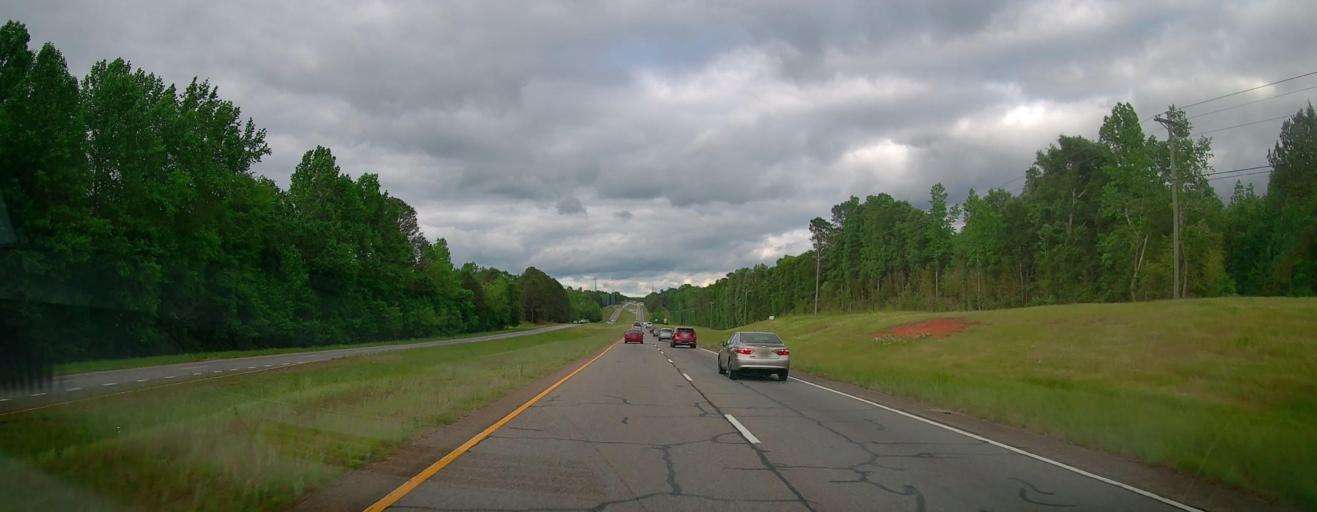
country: US
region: Georgia
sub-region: Oconee County
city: Bogart
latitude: 33.9038
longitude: -83.5691
